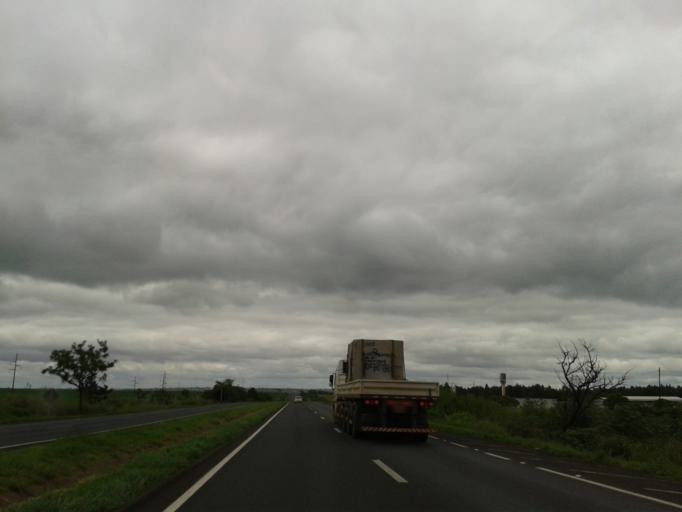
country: BR
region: Minas Gerais
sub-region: Uberlandia
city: Uberlandia
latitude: -19.0410
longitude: -48.1991
